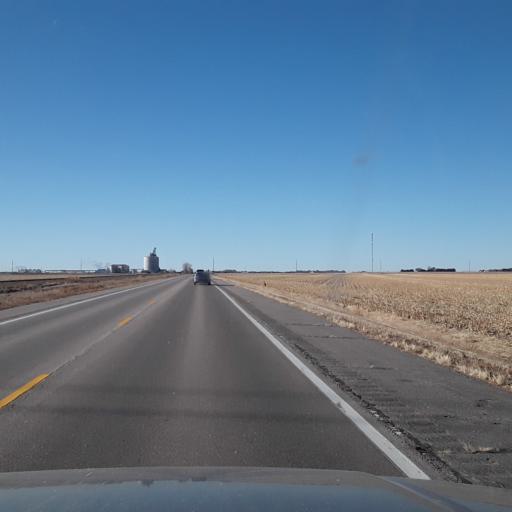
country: US
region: Nebraska
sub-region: Kearney County
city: Minden
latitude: 40.4880
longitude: -99.0564
